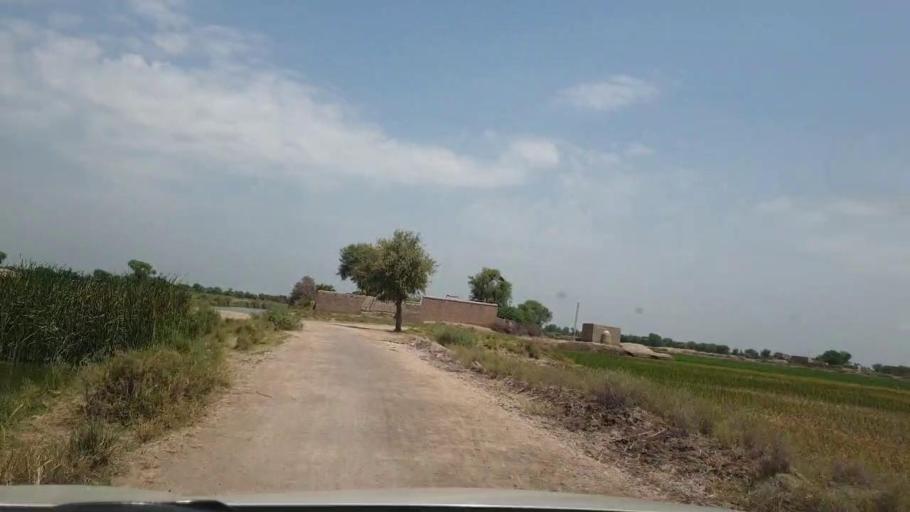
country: PK
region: Sindh
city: Ratodero
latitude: 27.8058
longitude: 68.2255
